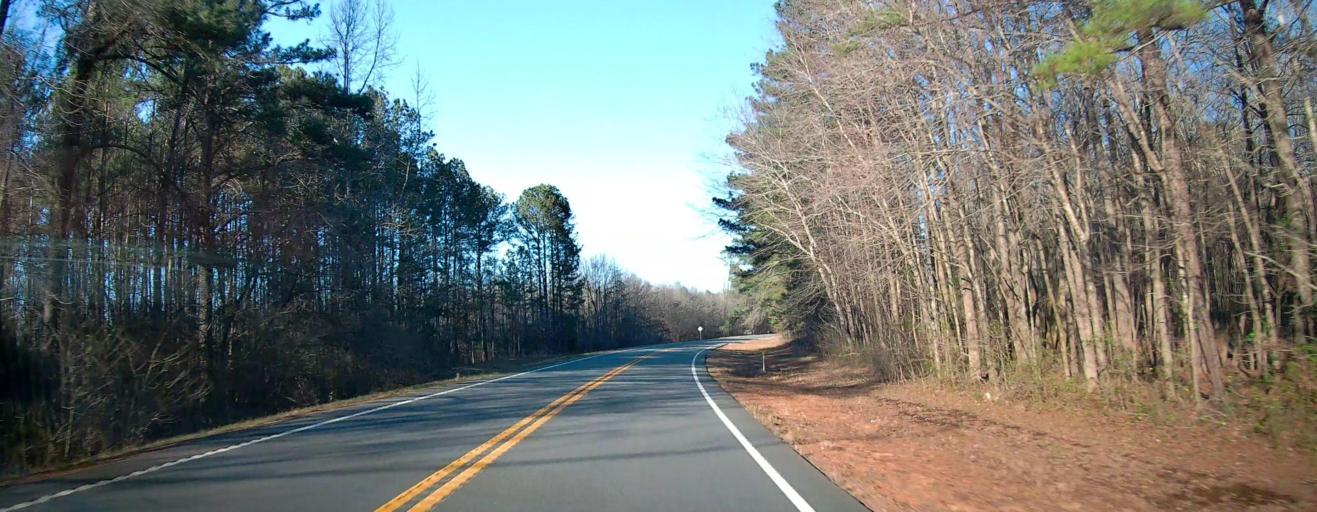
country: US
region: Georgia
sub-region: Meriwether County
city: Manchester
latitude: 32.9286
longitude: -84.6536
